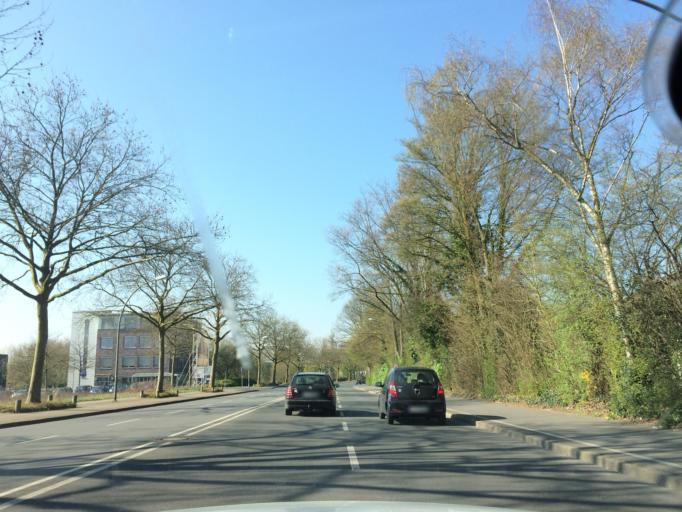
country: DE
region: North Rhine-Westphalia
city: Herten
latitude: 51.5677
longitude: 7.0769
